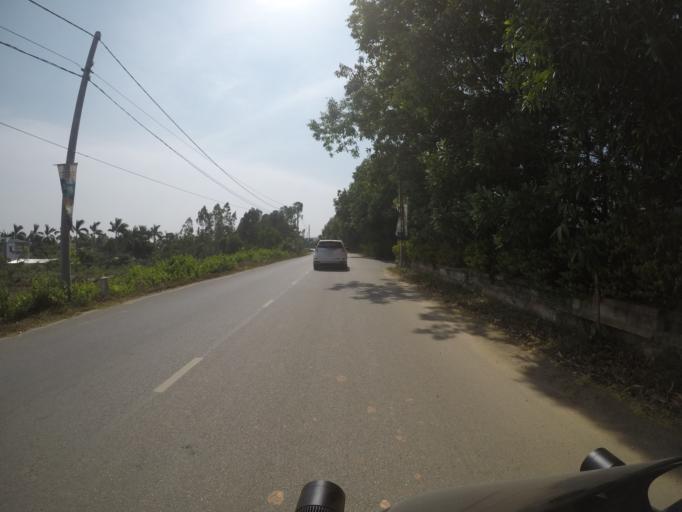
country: VN
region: Vinh Phuc
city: Phuc Yen
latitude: 21.3171
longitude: 105.7280
